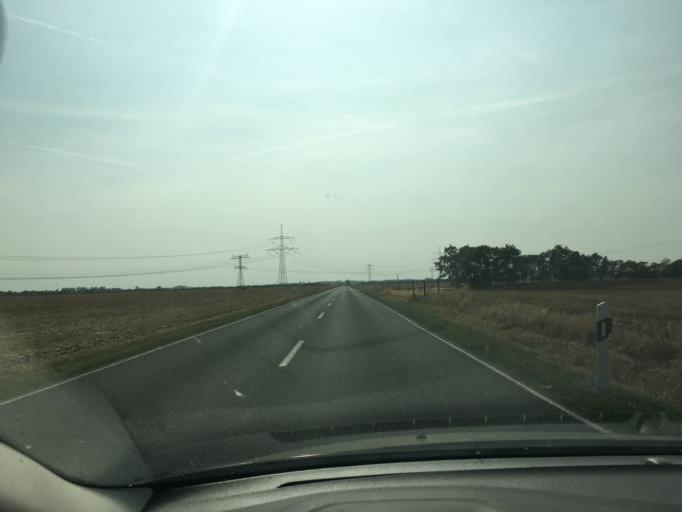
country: DE
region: Saxony-Anhalt
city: Barby
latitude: 51.9495
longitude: 11.8546
